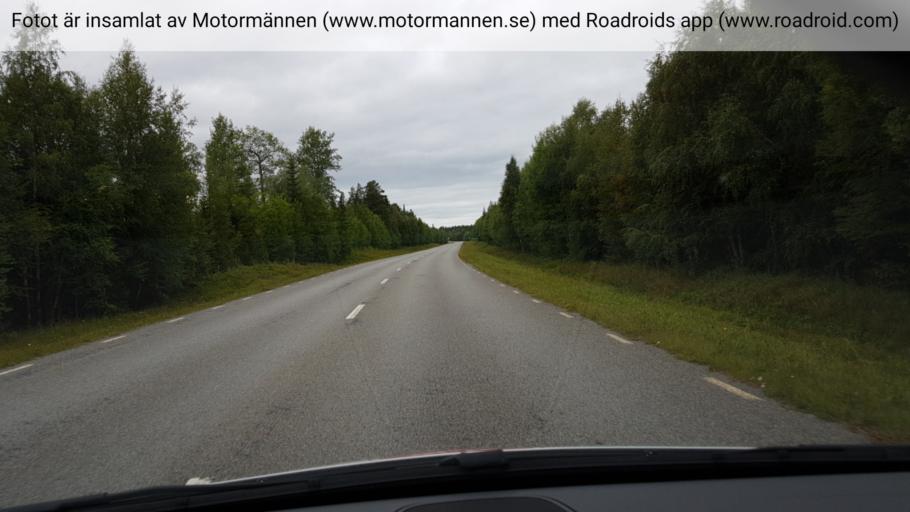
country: SE
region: Jaemtland
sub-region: Stroemsunds Kommun
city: Stroemsund
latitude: 64.3057
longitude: 15.2708
